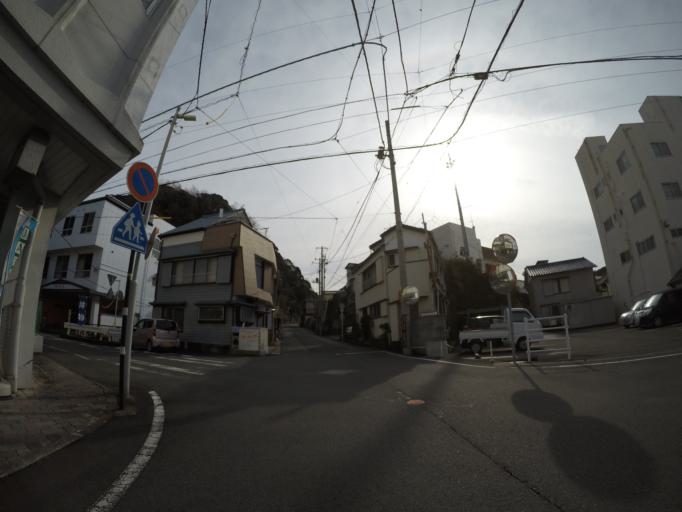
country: JP
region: Shizuoka
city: Heda
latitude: 34.8034
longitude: 138.7638
